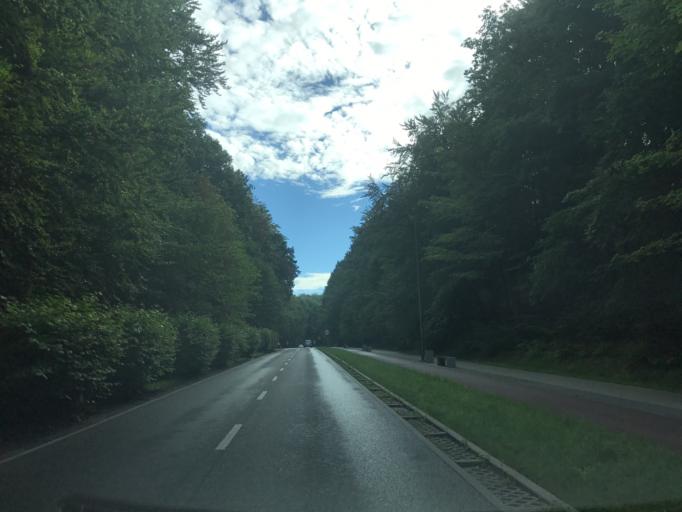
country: PL
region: West Pomeranian Voivodeship
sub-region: Koszalin
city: Koszalin
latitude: 54.2034
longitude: 16.2229
